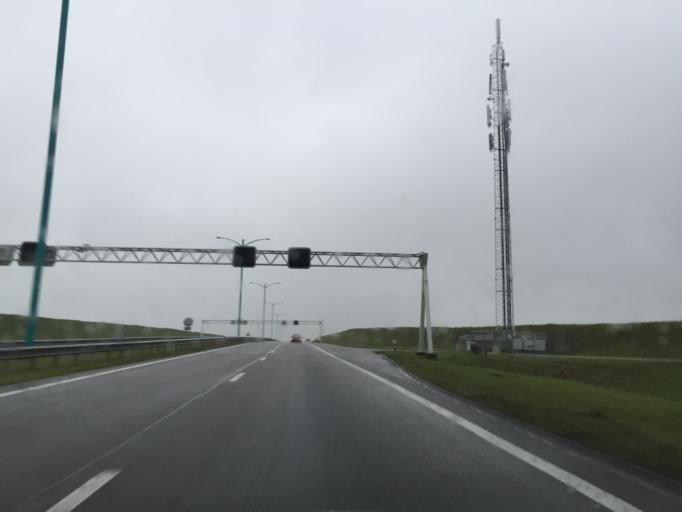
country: NL
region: Zeeland
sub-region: Gemeente Borsele
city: Borssele
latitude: 51.4011
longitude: 3.7928
